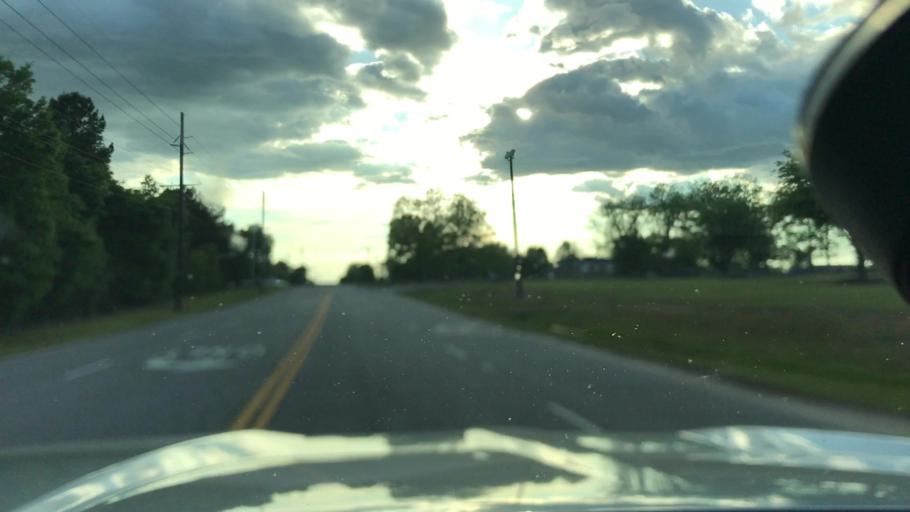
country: US
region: South Carolina
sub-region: Barnwell County
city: Blackville
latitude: 33.4740
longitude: -81.1878
